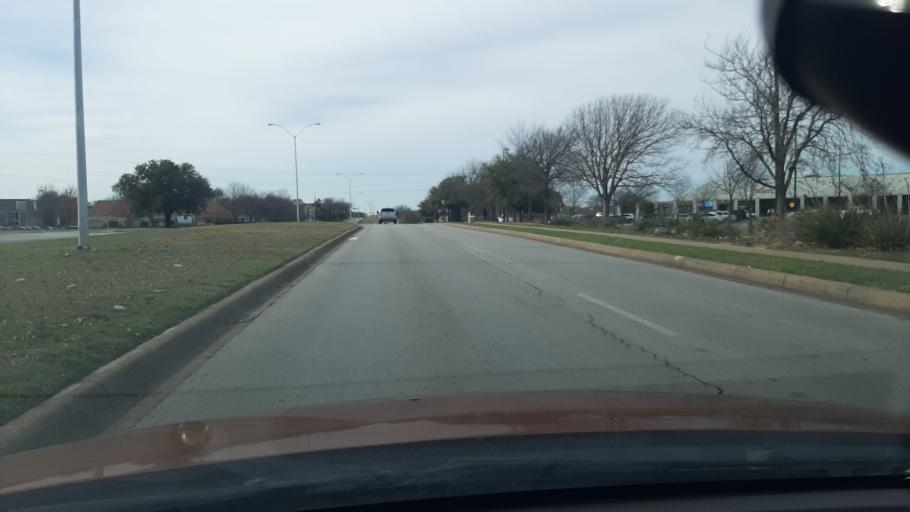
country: US
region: Texas
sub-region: Tarrant County
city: Benbrook
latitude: 32.6630
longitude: -97.4047
